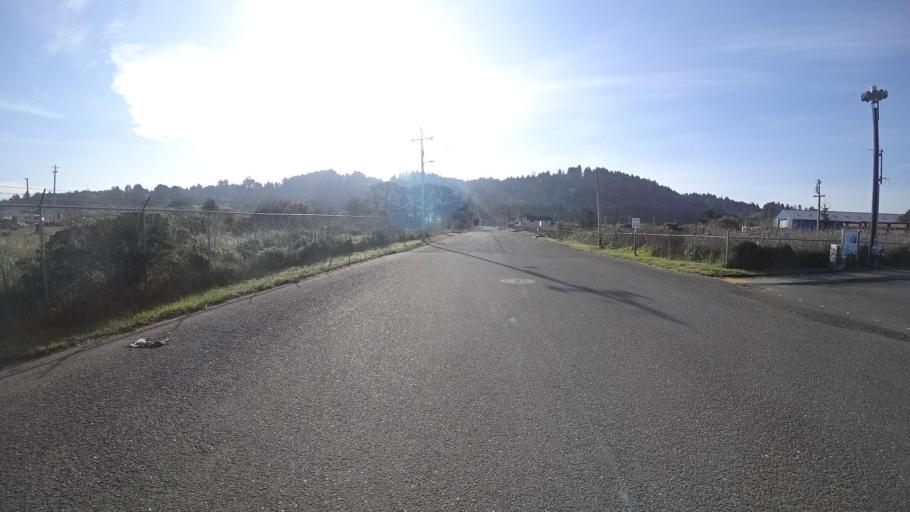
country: US
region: California
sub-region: Humboldt County
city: Humboldt Hill
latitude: 40.7259
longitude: -124.2202
